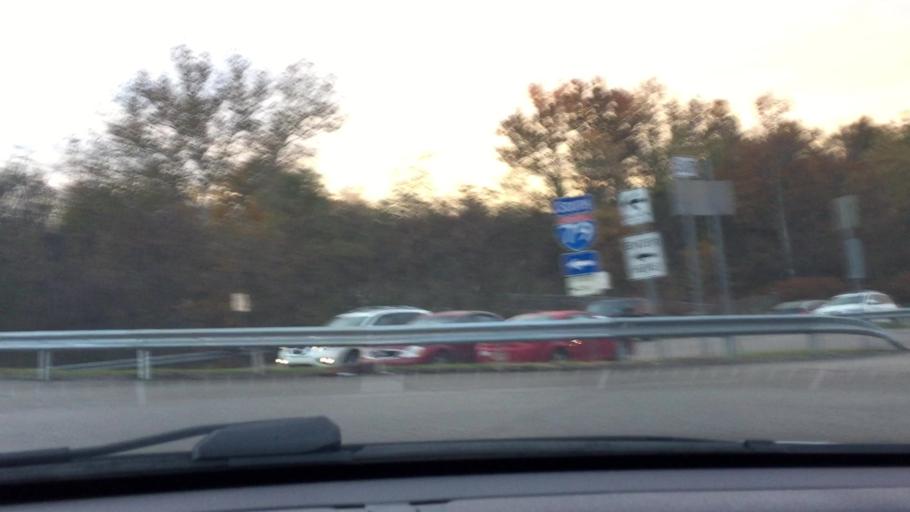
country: US
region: Pennsylvania
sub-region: Washington County
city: Houston
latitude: 40.2458
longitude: -80.2028
